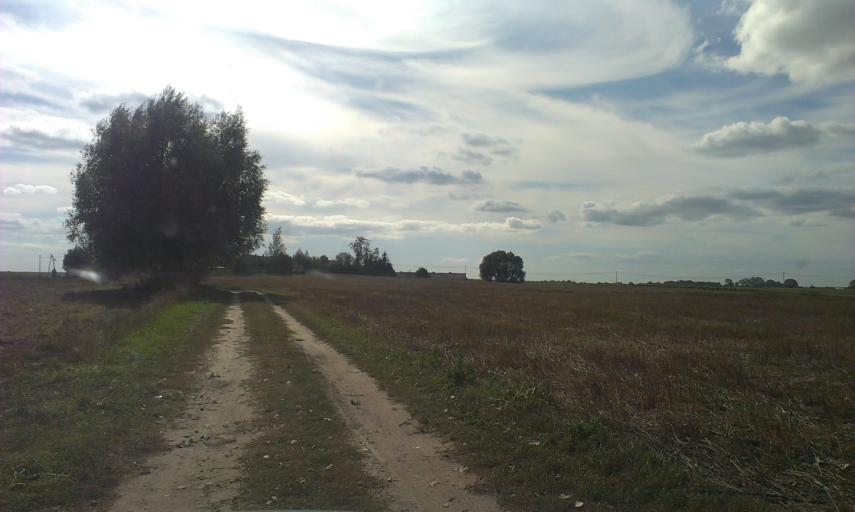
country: PL
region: Greater Poland Voivodeship
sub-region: Powiat zlotowski
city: Zakrzewo
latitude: 53.3016
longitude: 17.1475
